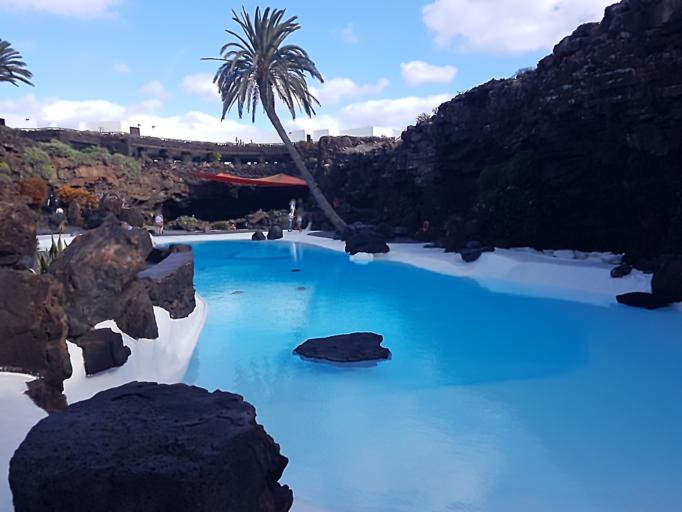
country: ES
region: Canary Islands
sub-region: Provincia de Las Palmas
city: Haria
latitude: 29.1573
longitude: -13.4324
